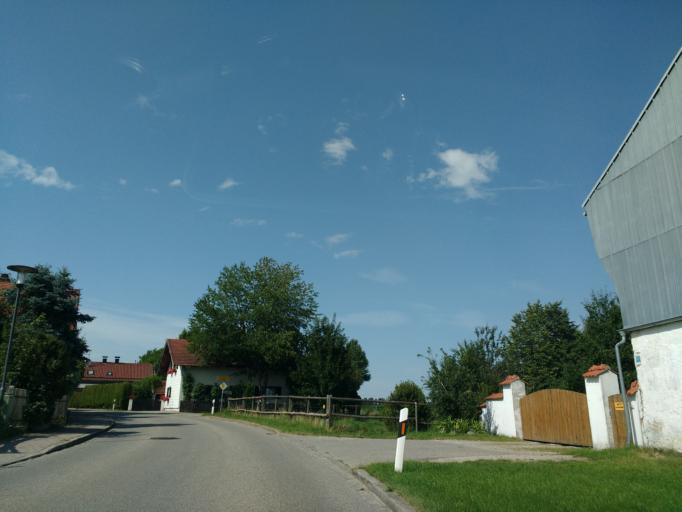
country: DE
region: Bavaria
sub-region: Upper Bavaria
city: Schnaitsee
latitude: 48.0678
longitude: 12.4173
